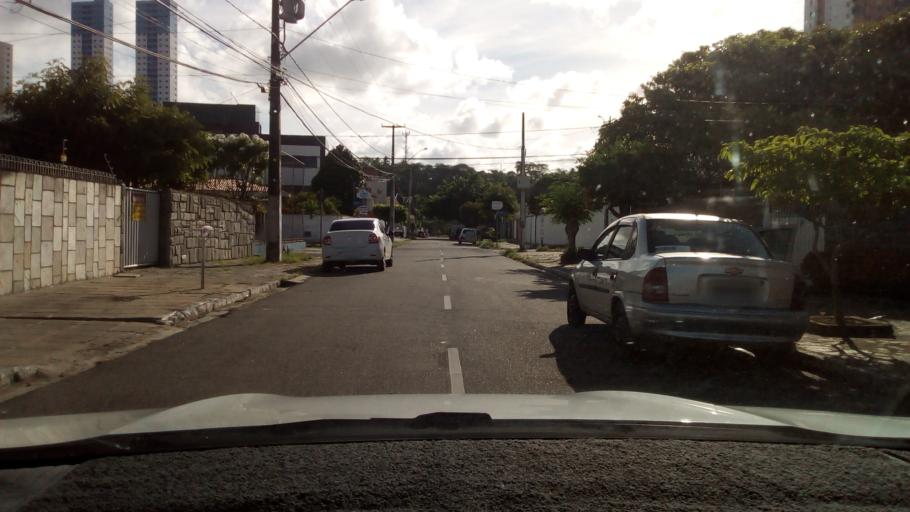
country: BR
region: Paraiba
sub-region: Joao Pessoa
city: Joao Pessoa
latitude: -7.1038
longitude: -34.8400
